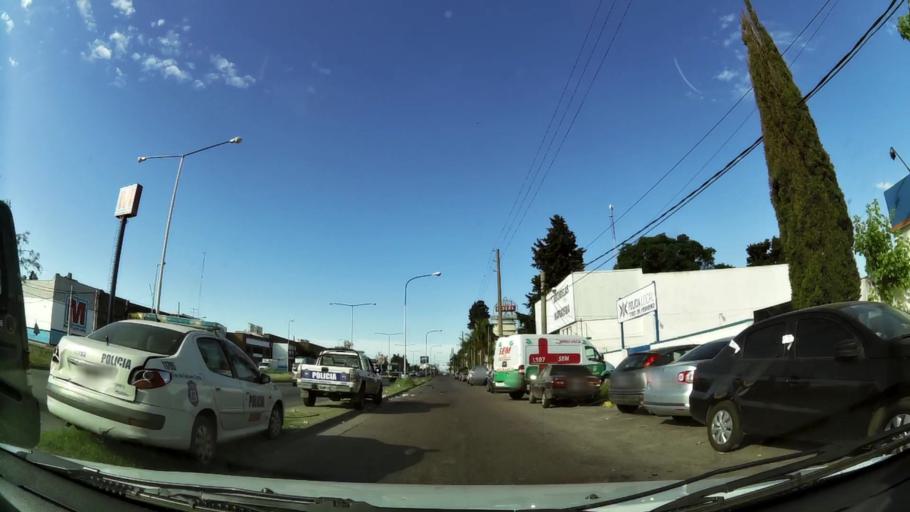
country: AR
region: Buenos Aires
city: Caseros
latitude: -34.5771
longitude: -58.5982
